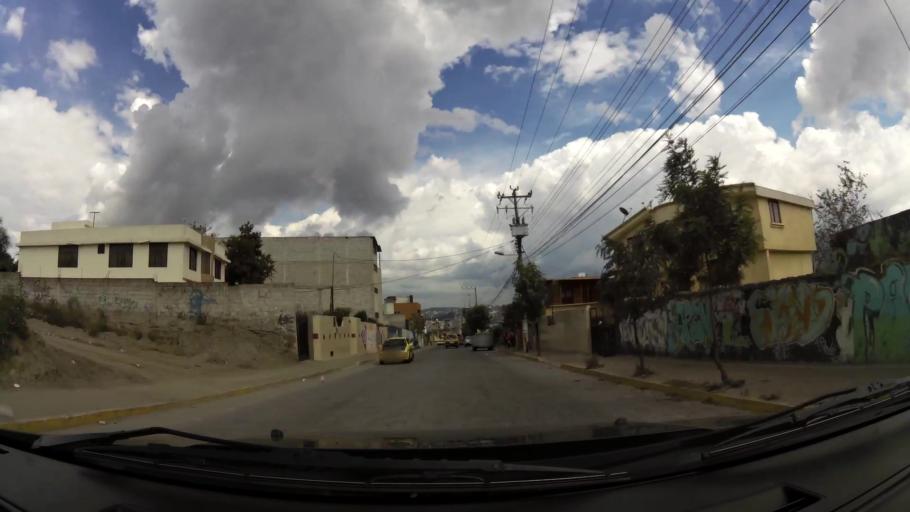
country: EC
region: Pichincha
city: Quito
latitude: -0.0812
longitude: -78.4364
